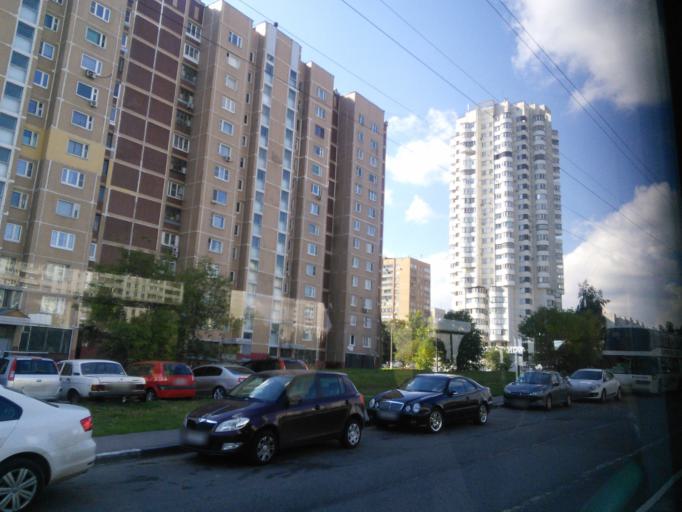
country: RU
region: Moscow
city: Tsaritsyno
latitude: 55.6380
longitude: 37.6603
